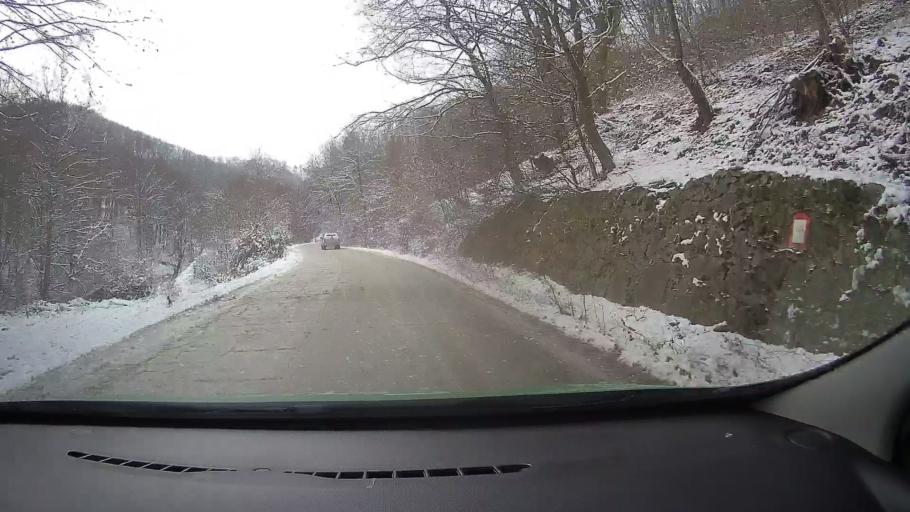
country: RO
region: Alba
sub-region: Oras Zlatna
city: Zlatna
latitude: 46.0979
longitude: 23.1836
